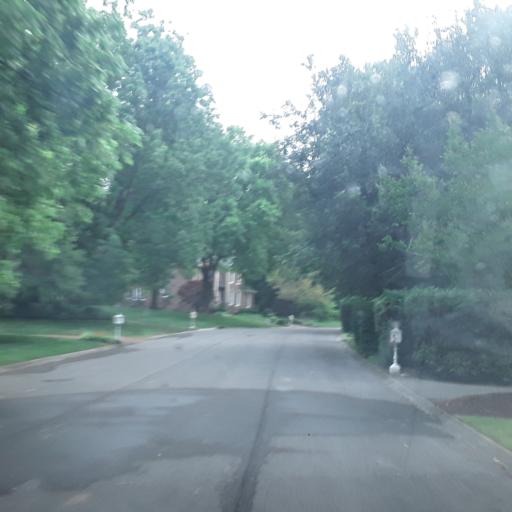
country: US
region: Tennessee
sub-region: Williamson County
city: Brentwood
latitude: 36.0461
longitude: -86.7712
